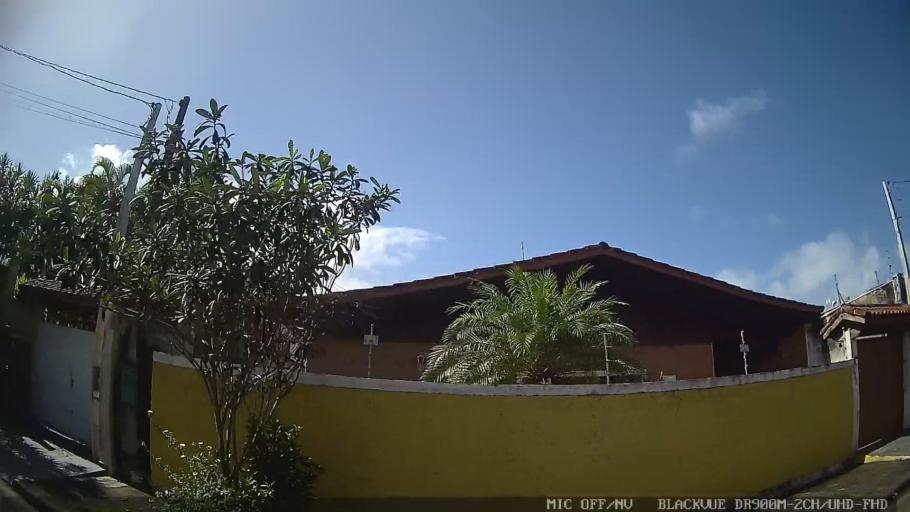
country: BR
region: Sao Paulo
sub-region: Itanhaem
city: Itanhaem
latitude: -24.1680
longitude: -46.7607
